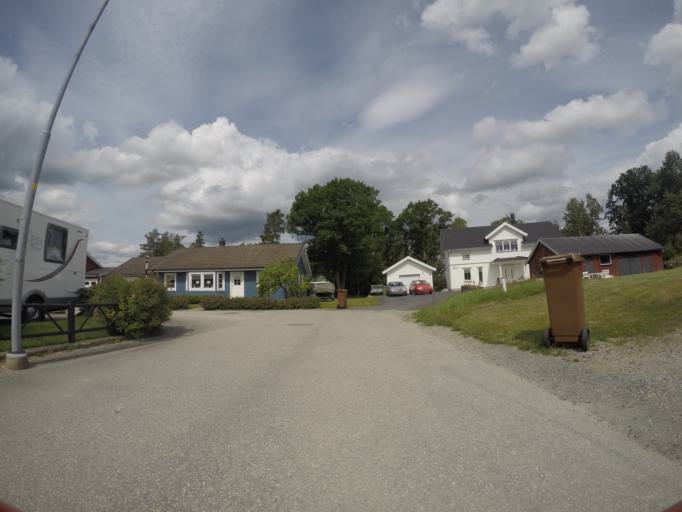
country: SE
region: Vaestra Goetaland
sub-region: Trollhattan
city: Trollhattan
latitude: 58.2298
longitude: 12.3039
